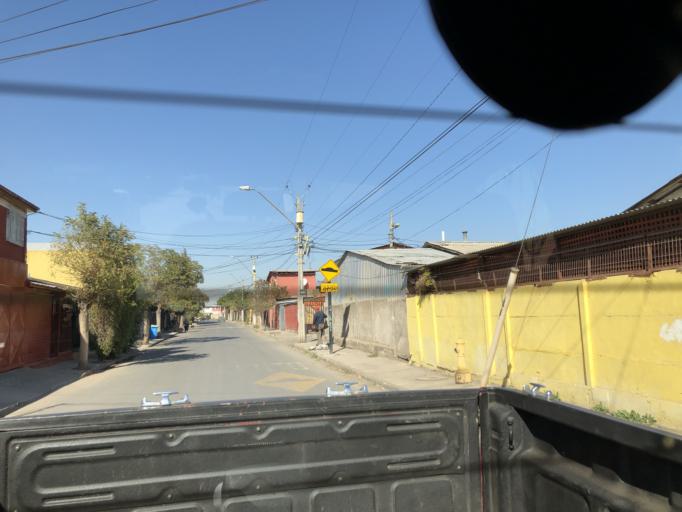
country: CL
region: Santiago Metropolitan
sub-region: Provincia de Cordillera
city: Puente Alto
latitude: -33.5655
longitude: -70.5662
